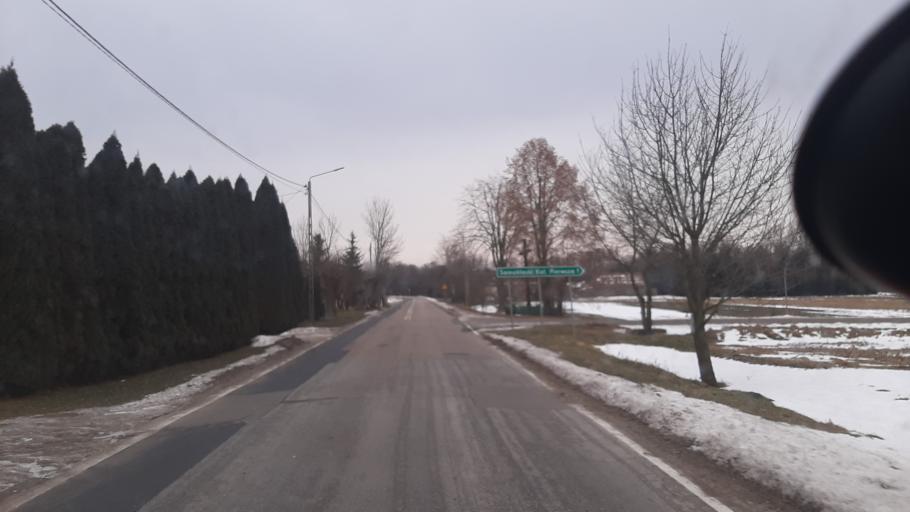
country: PL
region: Lublin Voivodeship
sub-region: Powiat lubartowski
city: Kamionka
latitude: 51.4505
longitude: 22.4215
